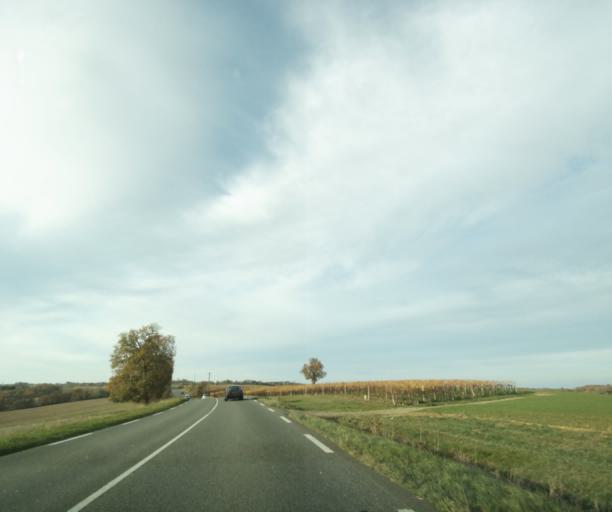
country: FR
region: Midi-Pyrenees
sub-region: Departement du Gers
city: Eauze
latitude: 43.7814
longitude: 0.1165
